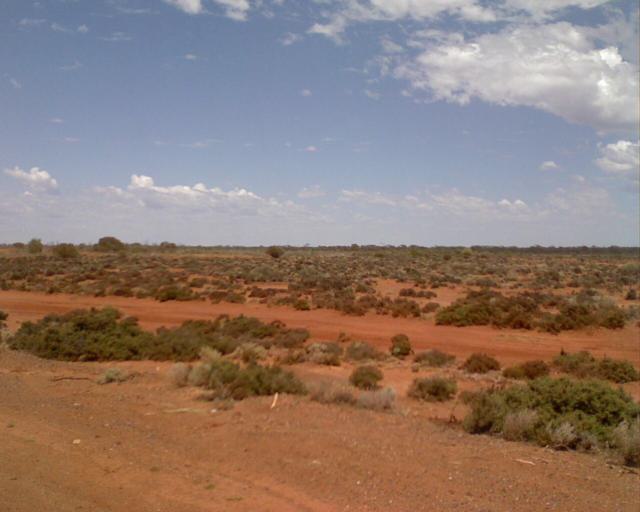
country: AU
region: Western Australia
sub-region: Kalgoorlie/Boulder
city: Stoneville
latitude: -31.2158
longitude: 121.6495
